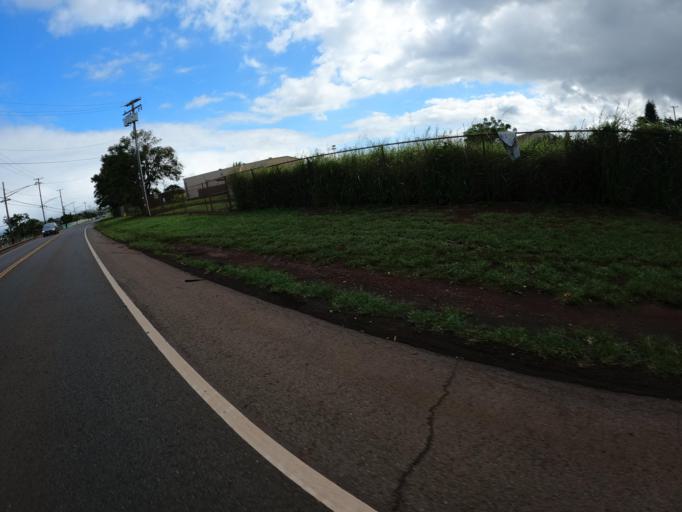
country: US
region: Hawaii
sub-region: Honolulu County
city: Whitmore Village
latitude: 21.5091
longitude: -158.0279
